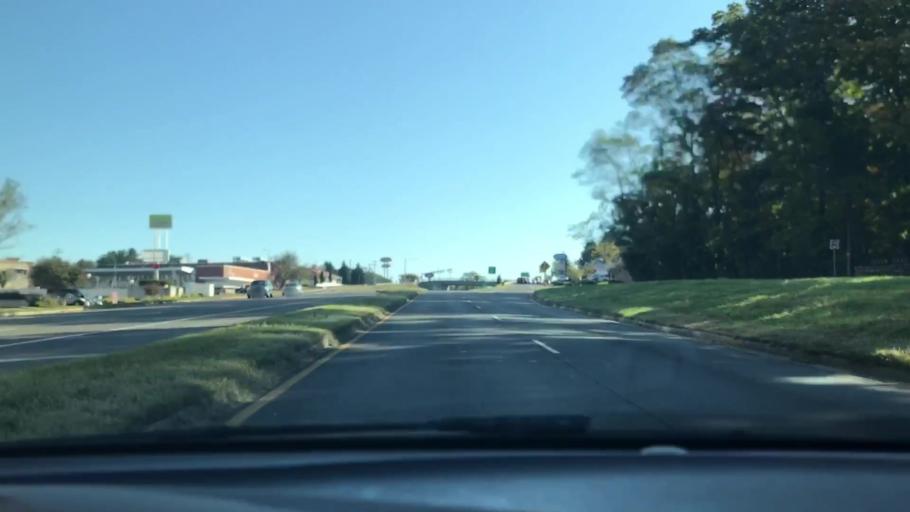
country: US
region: Virginia
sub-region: Fairfax County
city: Seven Corners
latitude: 38.8720
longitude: -77.1607
